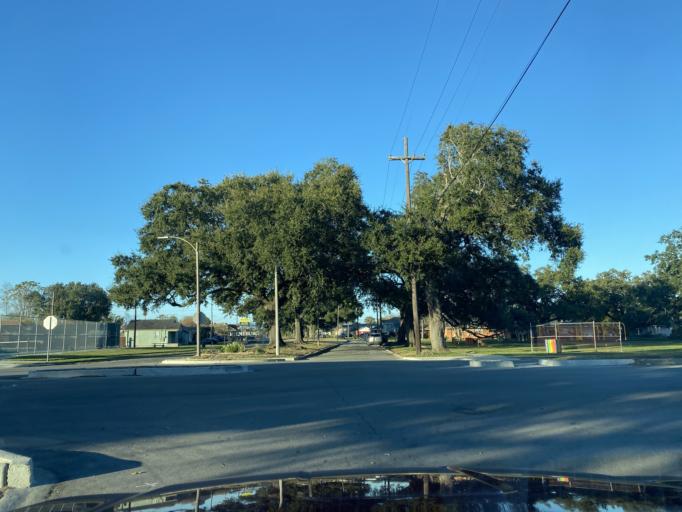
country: US
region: Louisiana
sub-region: Orleans Parish
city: New Orleans
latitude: 30.0130
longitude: -90.0558
